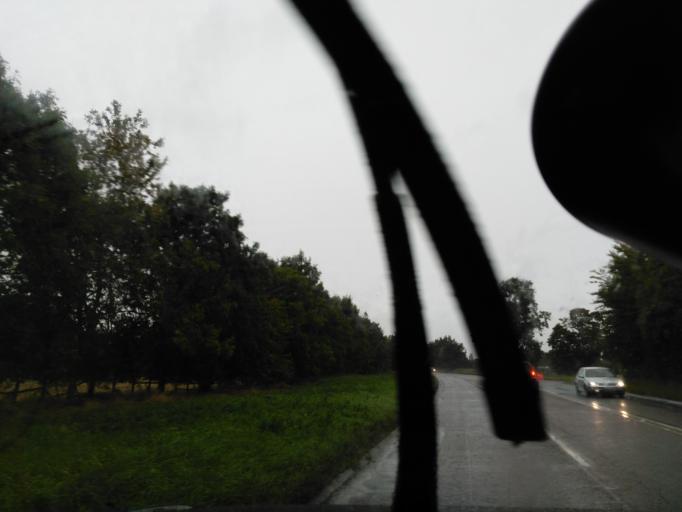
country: GB
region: England
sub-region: Wiltshire
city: Lacock
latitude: 51.4097
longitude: -2.1237
